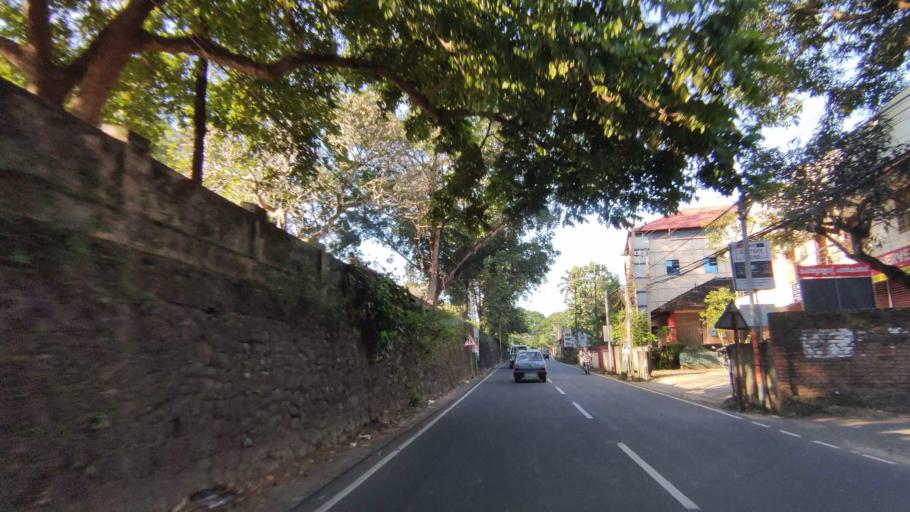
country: IN
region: Kerala
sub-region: Kottayam
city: Kottayam
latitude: 9.5985
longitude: 76.5172
